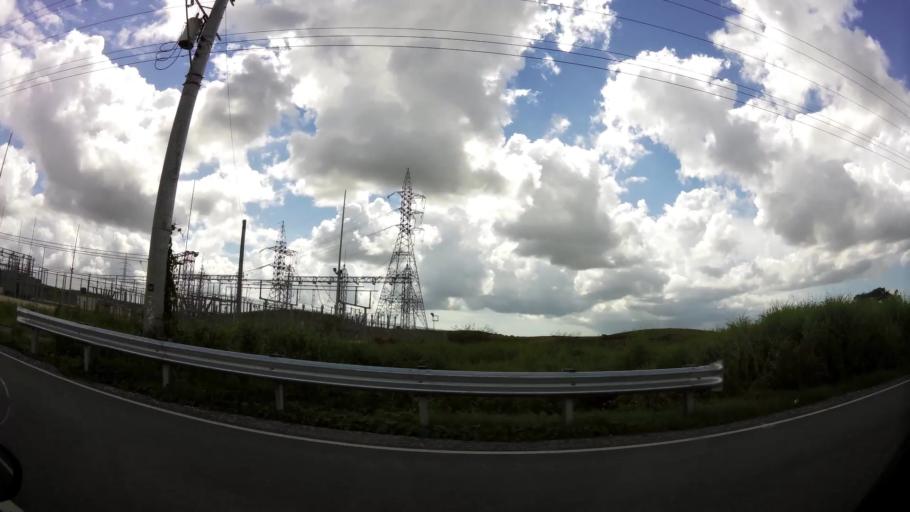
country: TT
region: Penal/Debe
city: Debe
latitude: 10.2183
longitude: -61.4702
